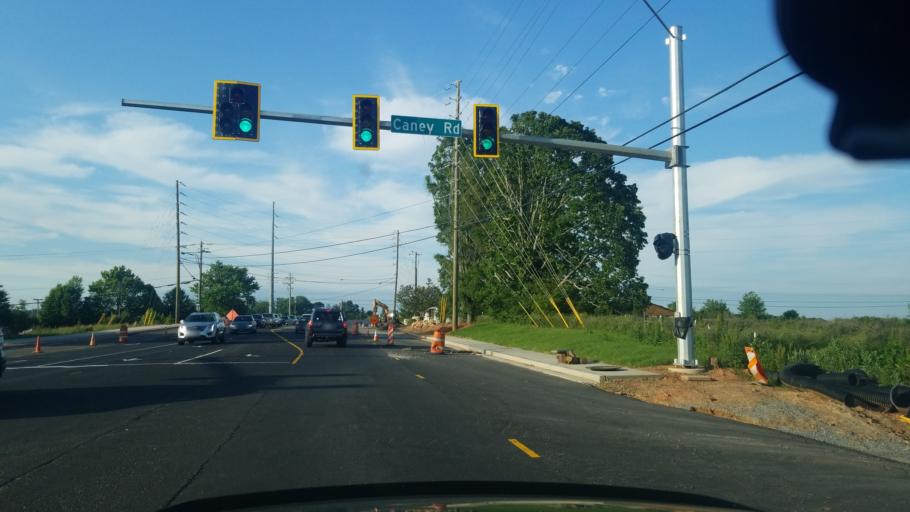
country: US
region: Georgia
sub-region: Fulton County
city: Johns Creek
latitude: 34.0942
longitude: -84.1779
